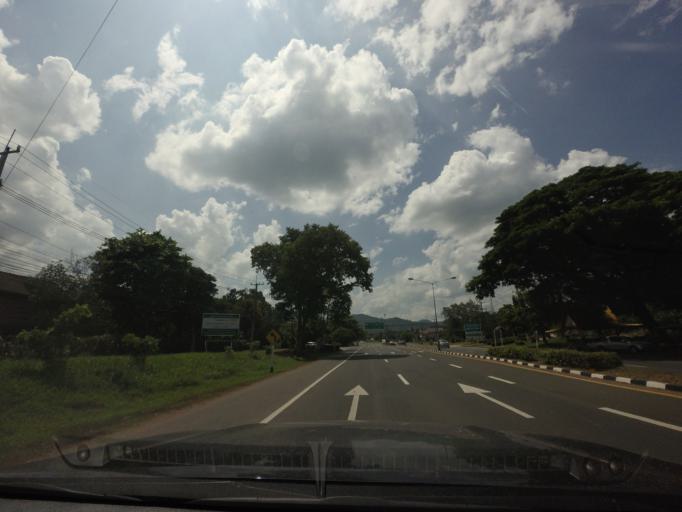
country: TH
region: Phetchabun
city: Phetchabun
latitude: 16.2658
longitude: 101.0504
